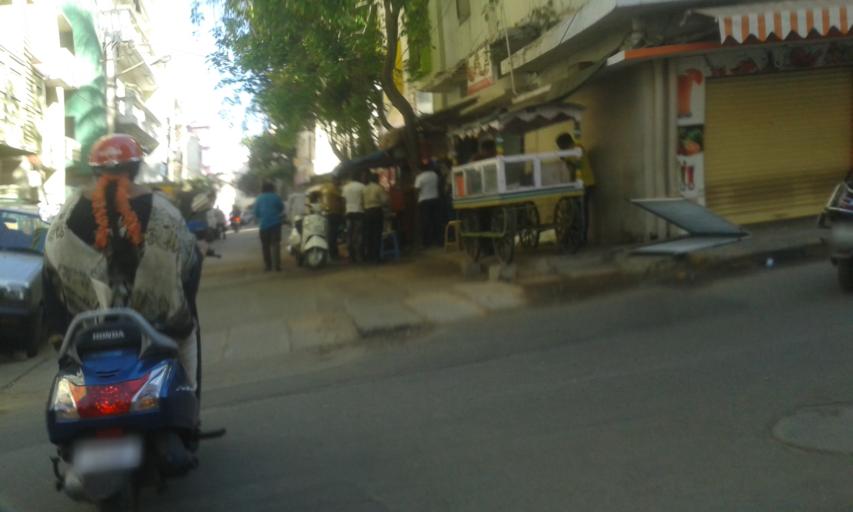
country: IN
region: Karnataka
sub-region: Bangalore Urban
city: Bangalore
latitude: 12.9418
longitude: 77.6077
